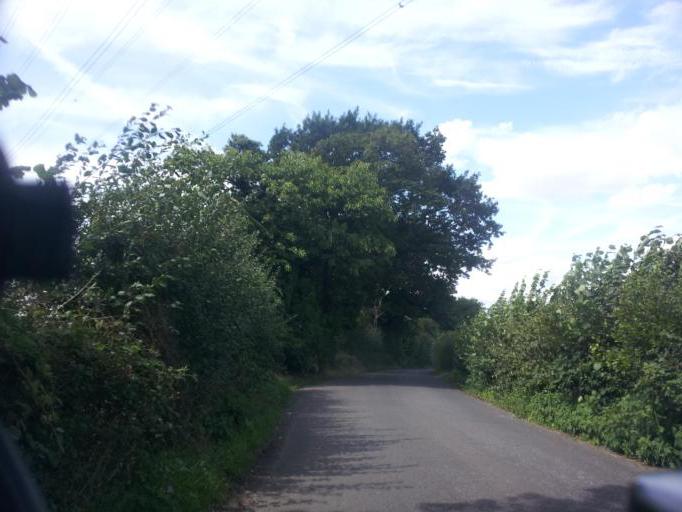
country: GB
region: England
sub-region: Kent
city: Newington
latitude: 51.3637
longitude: 0.6611
